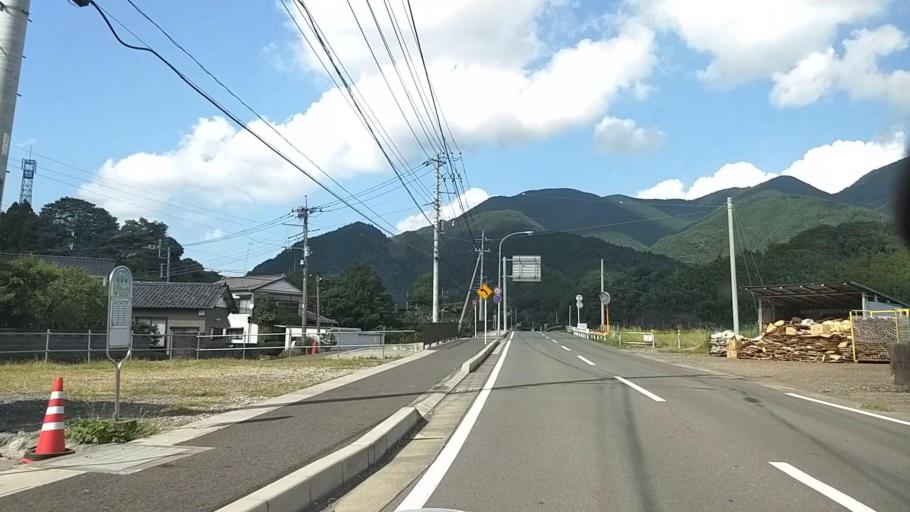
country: JP
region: Shizuoka
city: Fujinomiya
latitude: 35.2825
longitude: 138.4566
